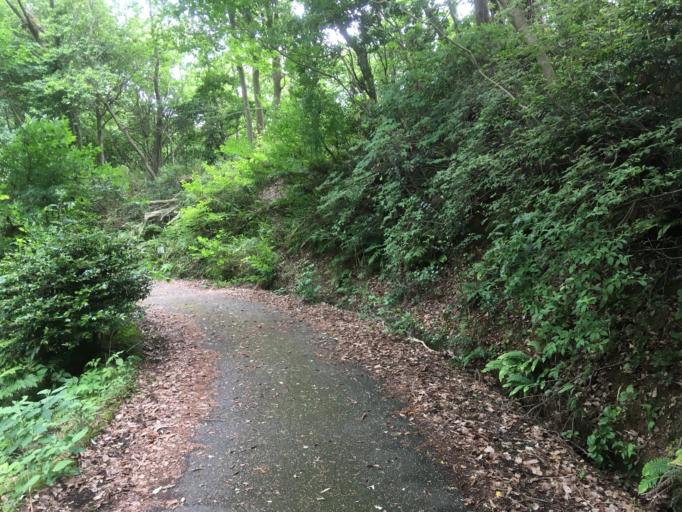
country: JP
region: Nara
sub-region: Ikoma-shi
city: Ikoma
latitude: 34.6947
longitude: 135.6712
